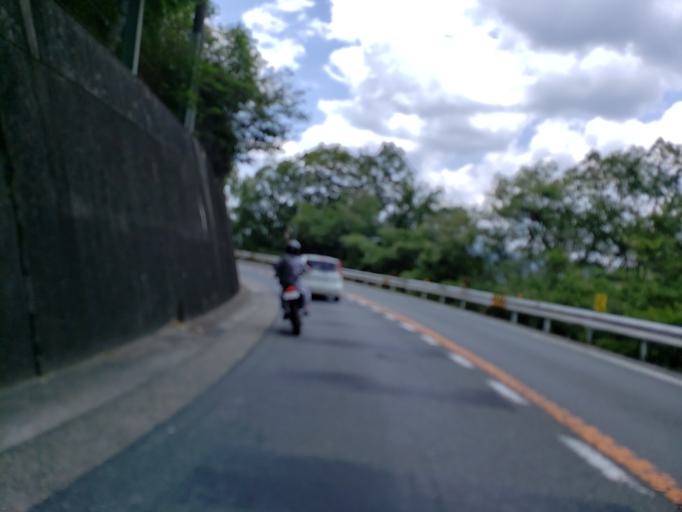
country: JP
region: Hyogo
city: Aioi
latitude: 34.7855
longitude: 134.4395
